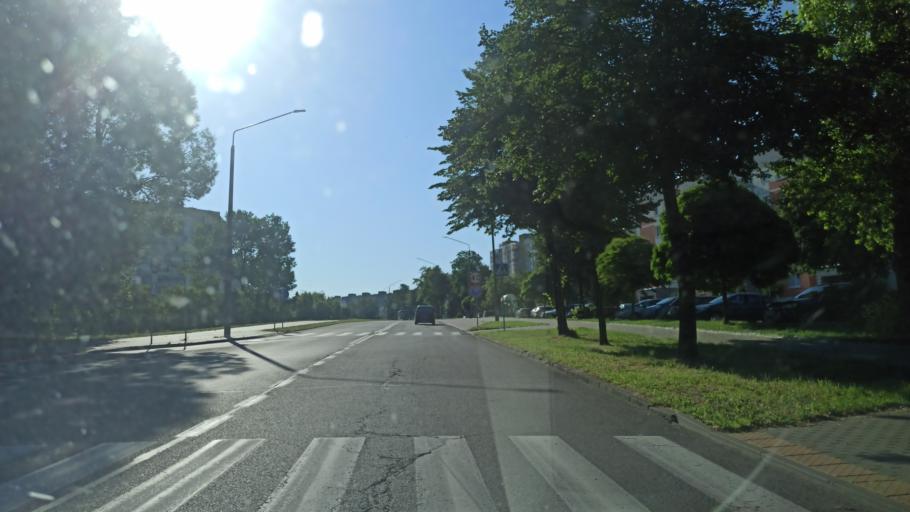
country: PL
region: Warmian-Masurian Voivodeship
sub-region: Powiat elblaski
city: Elblag
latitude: 54.1880
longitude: 19.3922
